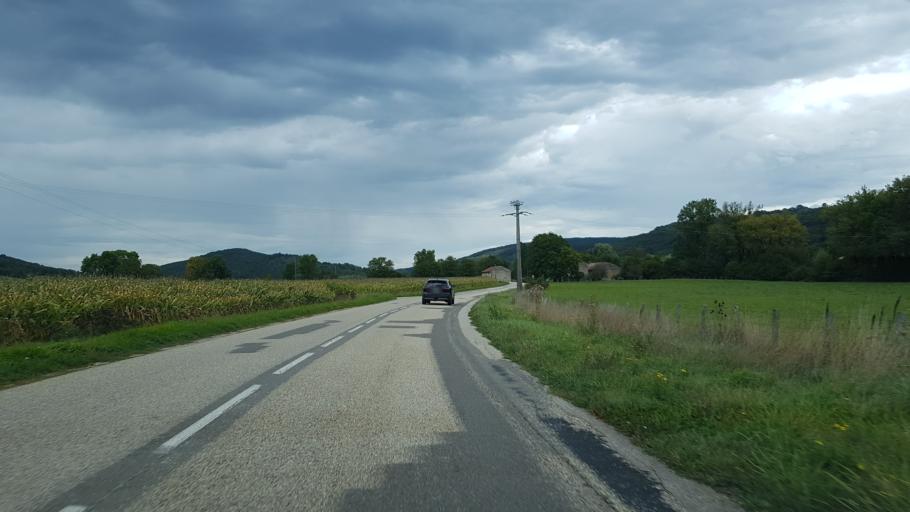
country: FR
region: Rhone-Alpes
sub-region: Departement de l'Ain
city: Cuisiat
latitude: 46.2896
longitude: 5.4318
